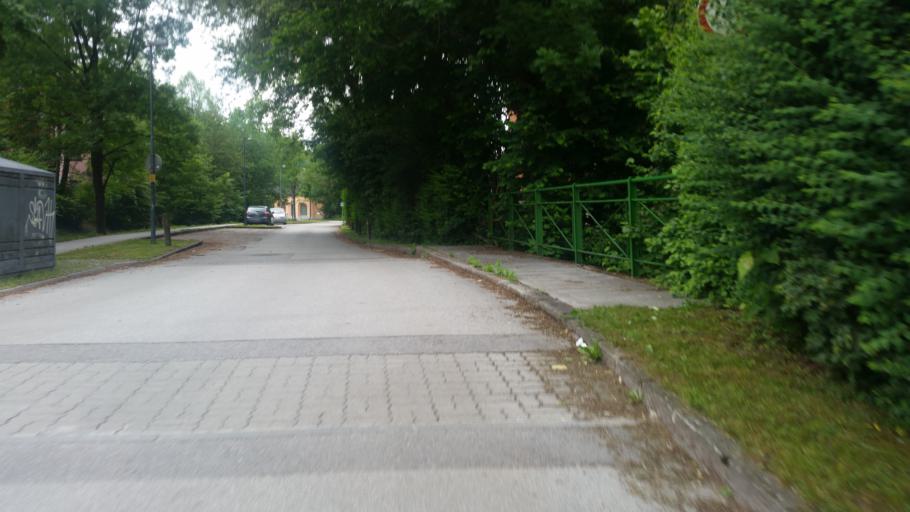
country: AT
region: Salzburg
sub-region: Salzburg Stadt
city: Salzburg
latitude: 47.7950
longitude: 13.0755
